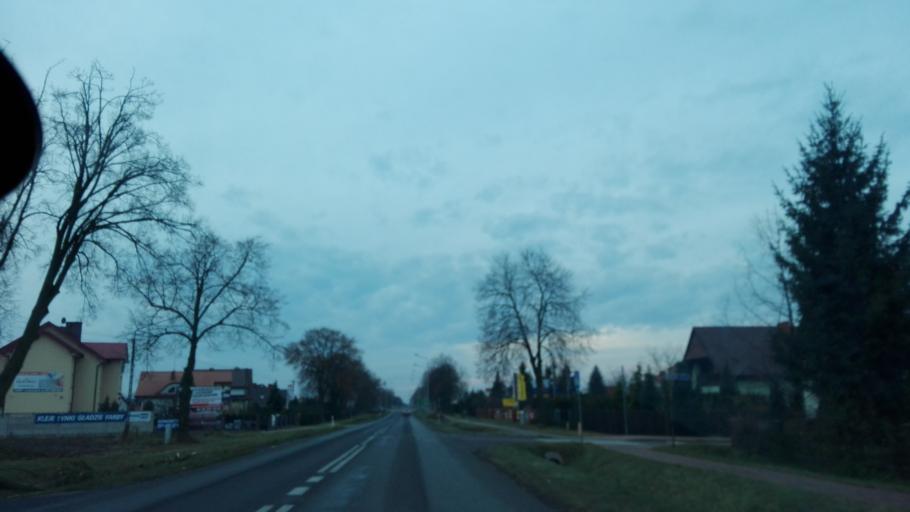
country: PL
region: Lublin Voivodeship
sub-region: Powiat radzynski
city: Radzyn Podlaski
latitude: 51.7742
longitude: 22.6263
